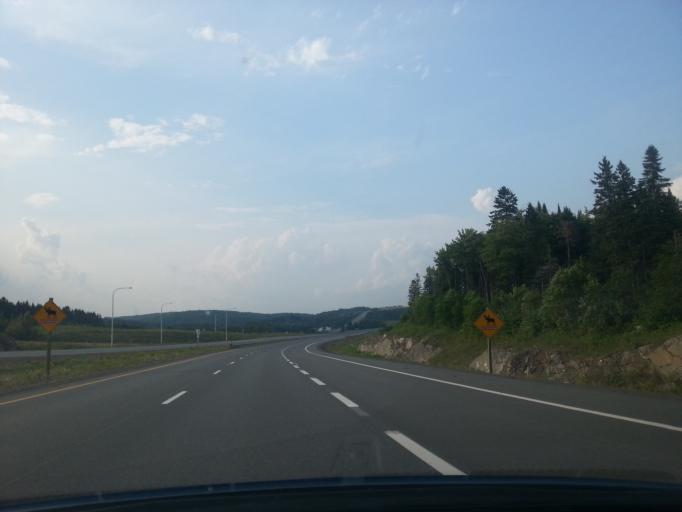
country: US
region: Maine
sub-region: Aroostook County
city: Fort Fairfield
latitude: 46.8162
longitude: -67.7321
